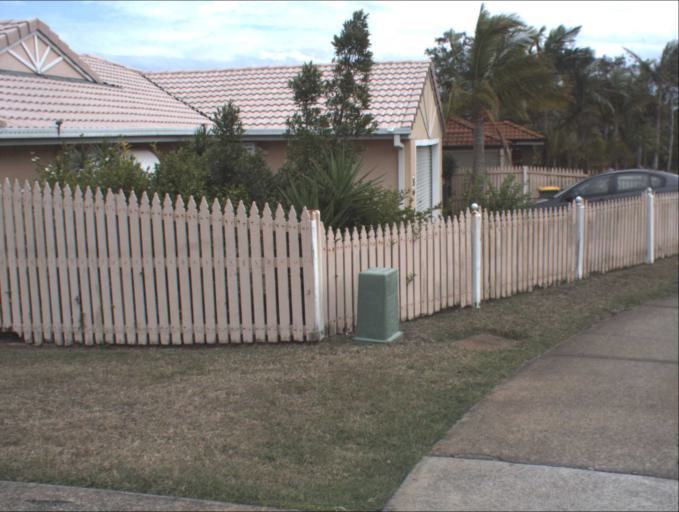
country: AU
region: Queensland
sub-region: Logan
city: Springwood
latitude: -27.6147
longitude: 153.1094
